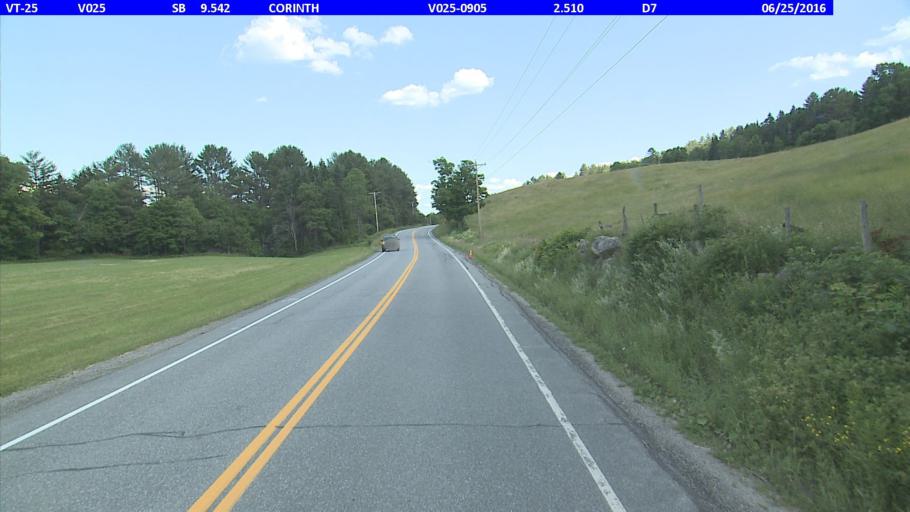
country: US
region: New Hampshire
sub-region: Grafton County
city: Haverhill
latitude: 44.0639
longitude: -72.2402
